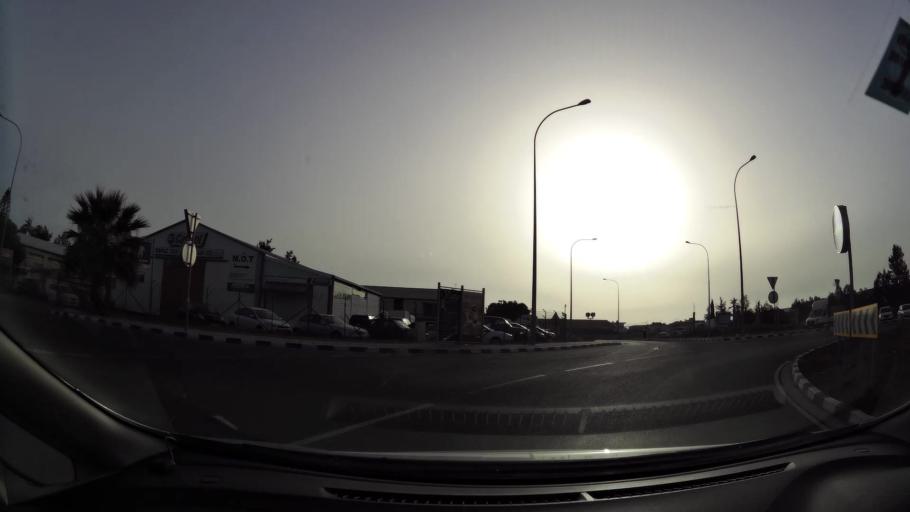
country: CY
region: Lefkosia
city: Geri
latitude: 35.0820
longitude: 33.3810
